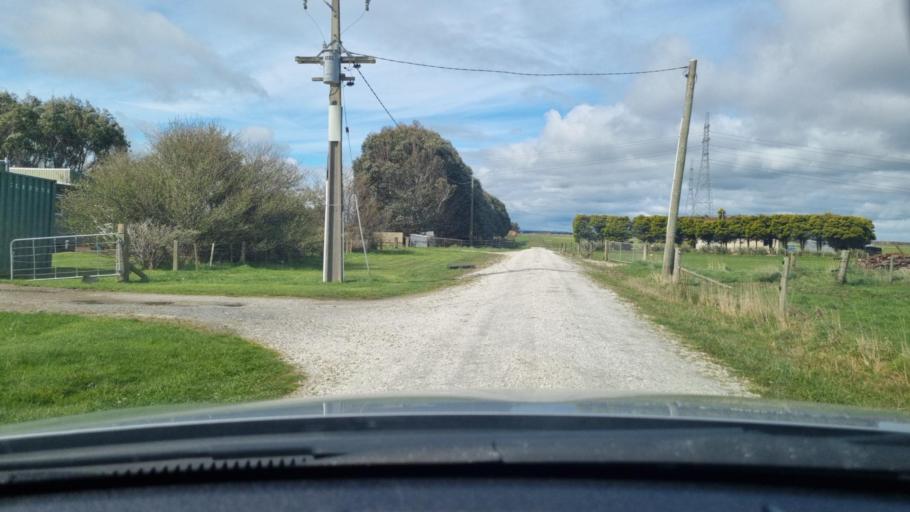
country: NZ
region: Southland
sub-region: Invercargill City
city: Invercargill
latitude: -46.4768
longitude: 168.4328
